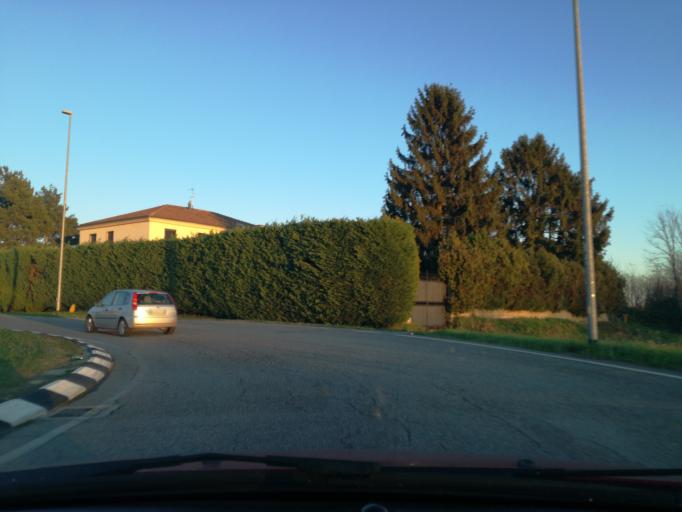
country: IT
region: Lombardy
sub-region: Provincia di Monza e Brianza
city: Carnate
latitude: 45.6471
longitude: 9.3863
